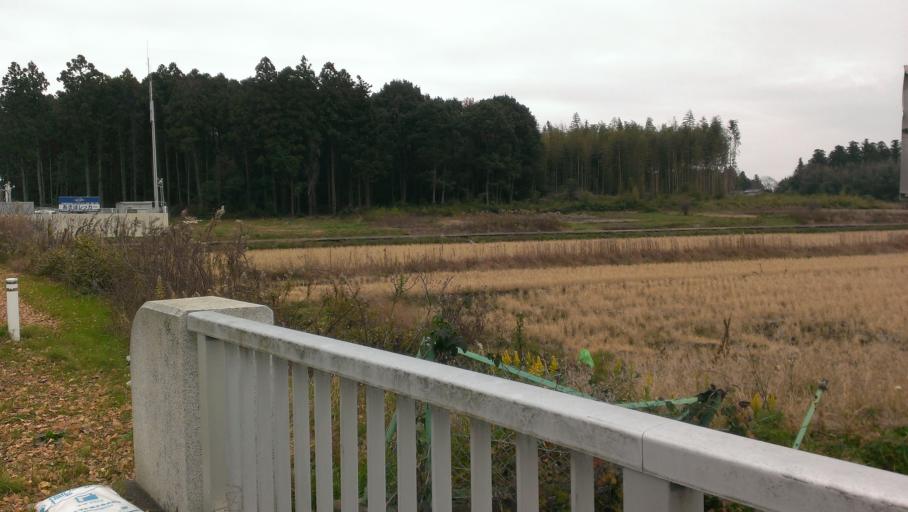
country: JP
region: Ibaraki
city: Naka
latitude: 36.1035
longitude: 140.0906
